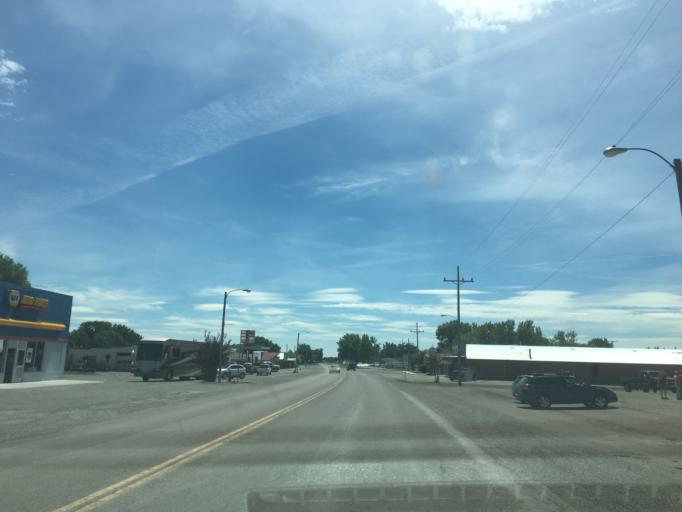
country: US
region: Montana
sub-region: Teton County
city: Choteau
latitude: 47.8081
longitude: -112.1801
